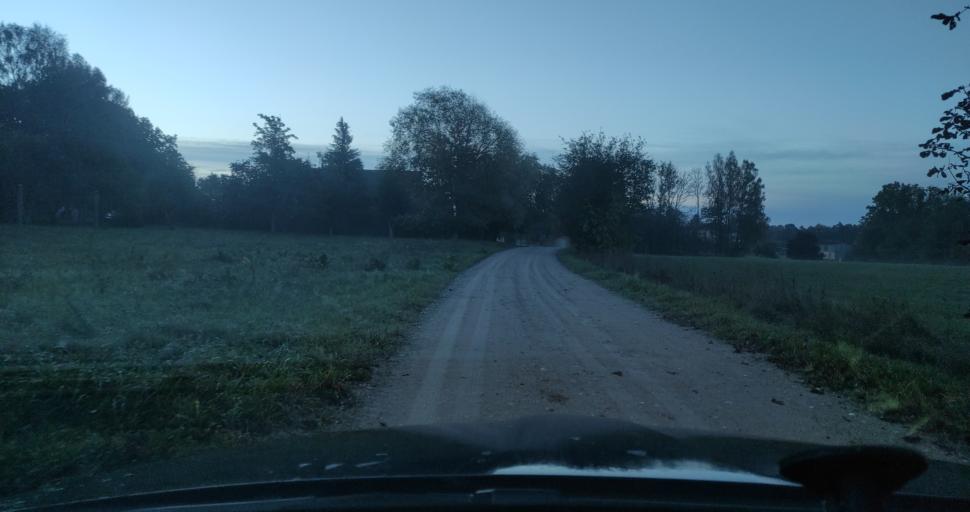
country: LV
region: Kuldigas Rajons
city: Kuldiga
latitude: 56.8854
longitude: 21.8172
